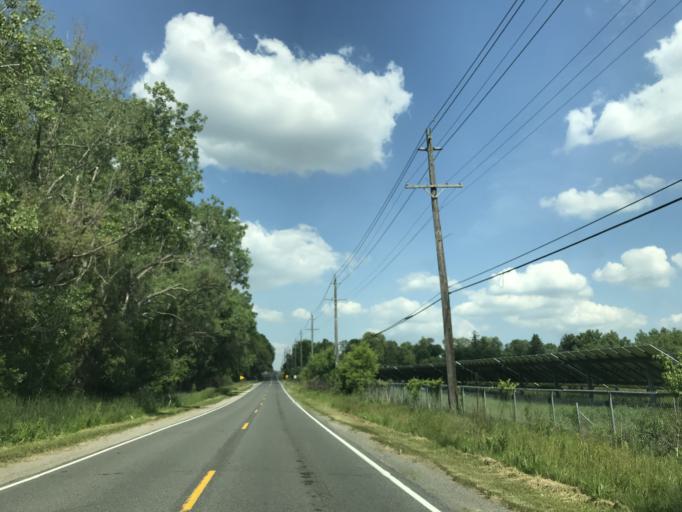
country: US
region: Michigan
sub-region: Washtenaw County
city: Ypsilanti
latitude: 42.2607
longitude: -83.6122
